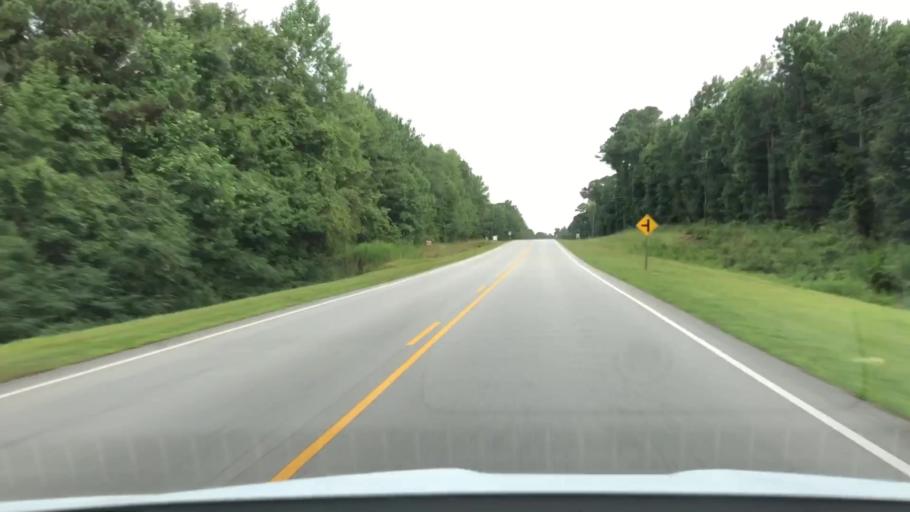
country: US
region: North Carolina
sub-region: Jones County
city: Trenton
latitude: 35.0100
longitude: -77.2873
